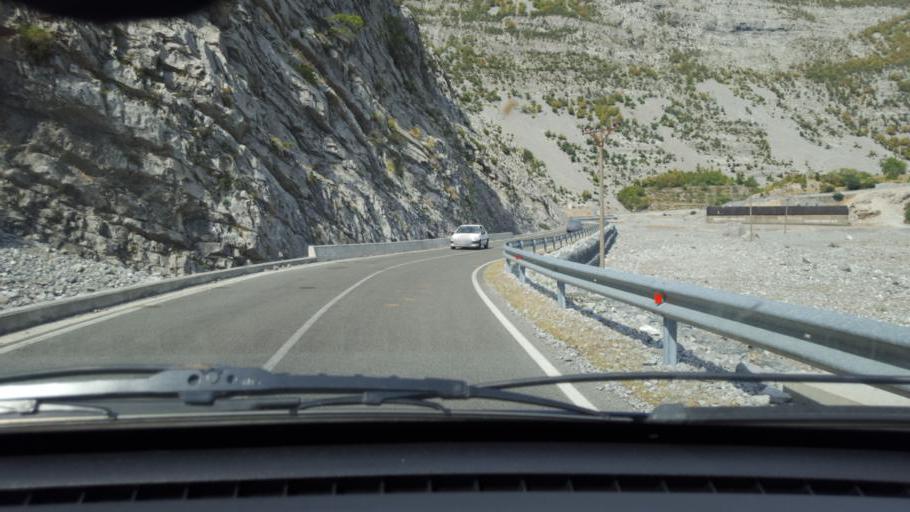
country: AL
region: Shkoder
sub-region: Rrethi i Malesia e Madhe
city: Kastrat
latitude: 42.4955
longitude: 19.5810
